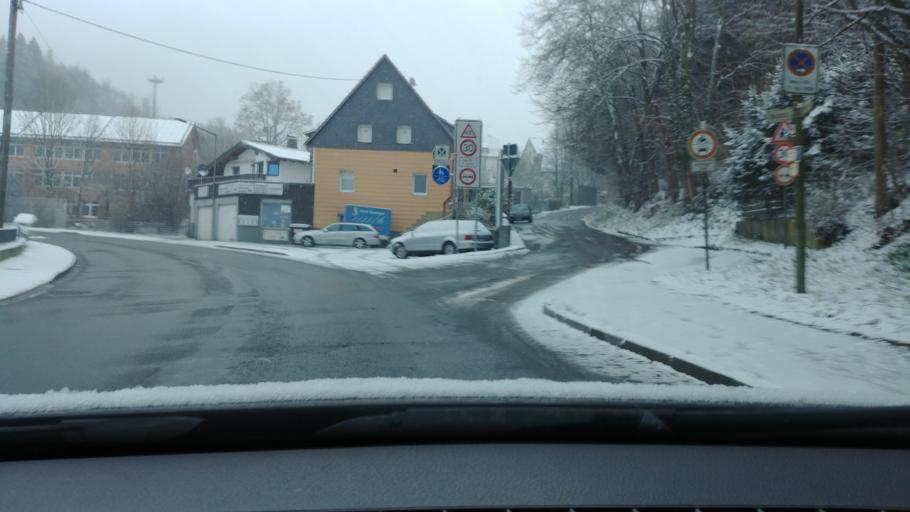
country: DE
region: North Rhine-Westphalia
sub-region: Regierungsbezirk Koln
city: Gummersbach
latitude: 51.0398
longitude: 7.5948
